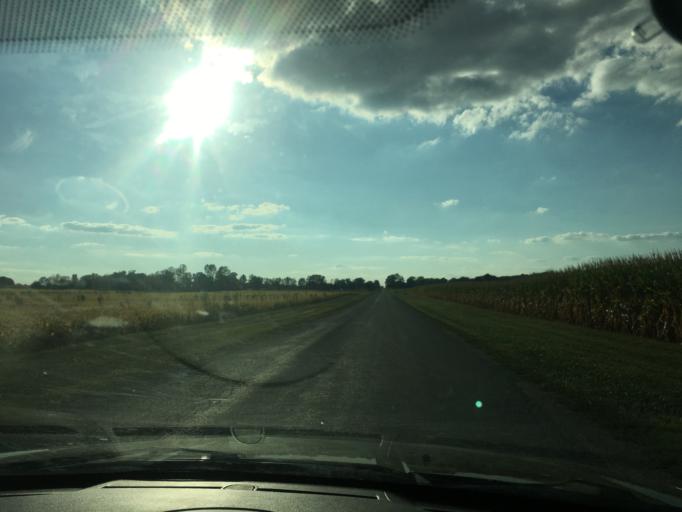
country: US
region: Ohio
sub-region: Logan County
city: West Liberty
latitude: 40.1841
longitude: -83.7432
